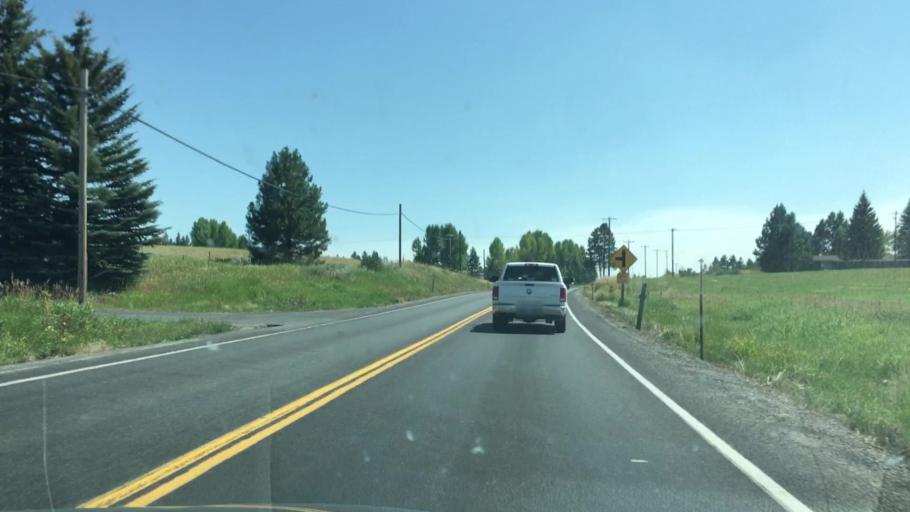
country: US
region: Idaho
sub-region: Valley County
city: McCall
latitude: 44.8850
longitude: -116.0912
